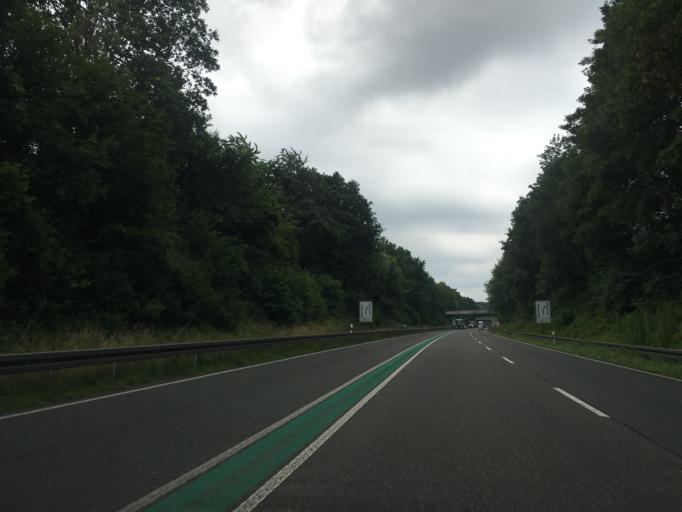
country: DE
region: North Rhine-Westphalia
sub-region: Regierungsbezirk Munster
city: Steinfurt
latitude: 52.1549
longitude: 7.3512
